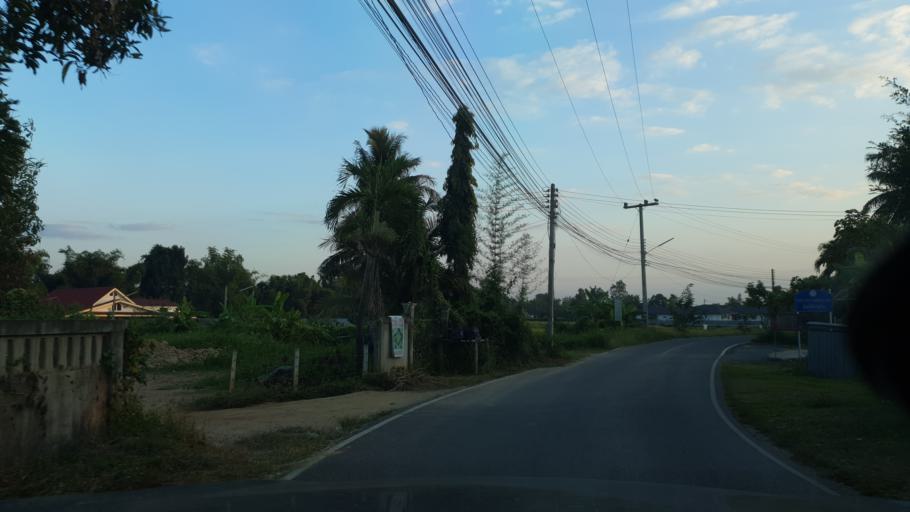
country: TH
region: Chiang Mai
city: San Sai
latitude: 18.8577
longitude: 99.0748
